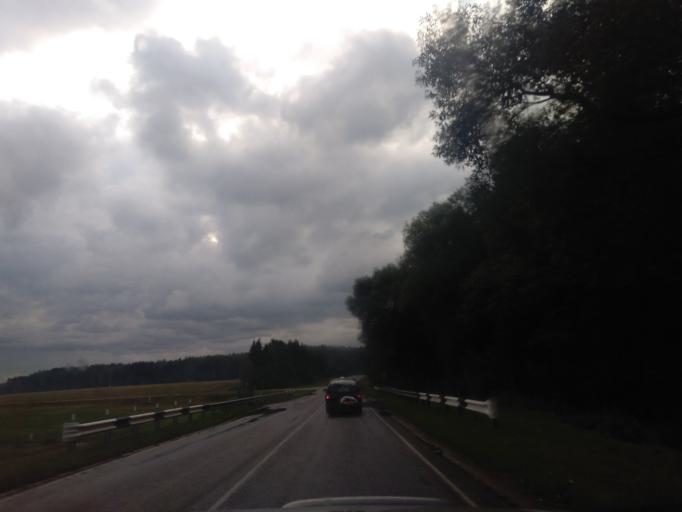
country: BY
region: Minsk
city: Enyerhyetykaw
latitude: 53.5411
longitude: 27.0603
